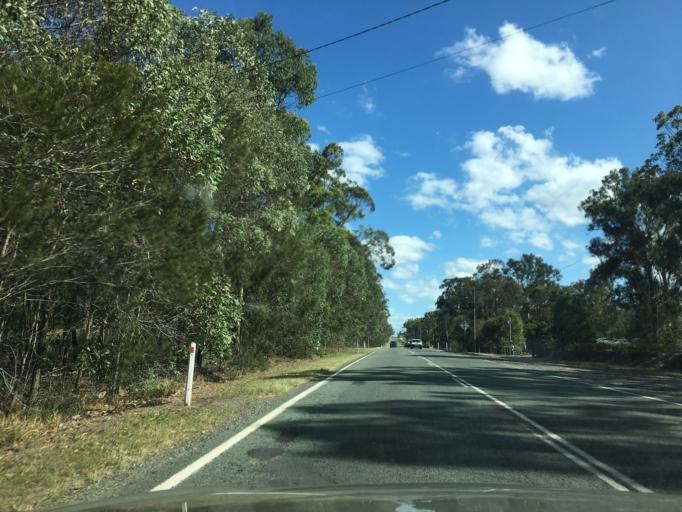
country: AU
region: Queensland
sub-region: Logan
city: Logan Reserve
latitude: -27.7328
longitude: 153.1288
